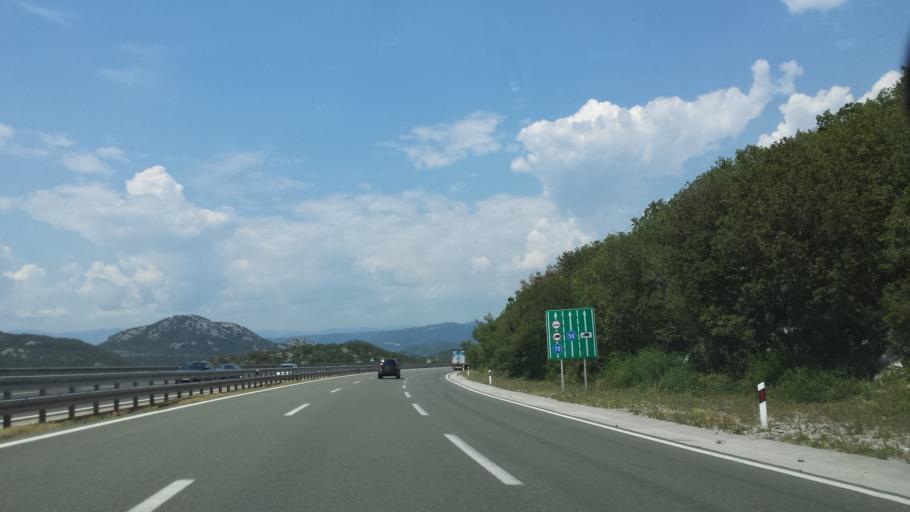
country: HR
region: Primorsko-Goranska
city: Skrljevo
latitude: 45.3618
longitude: 14.5558
